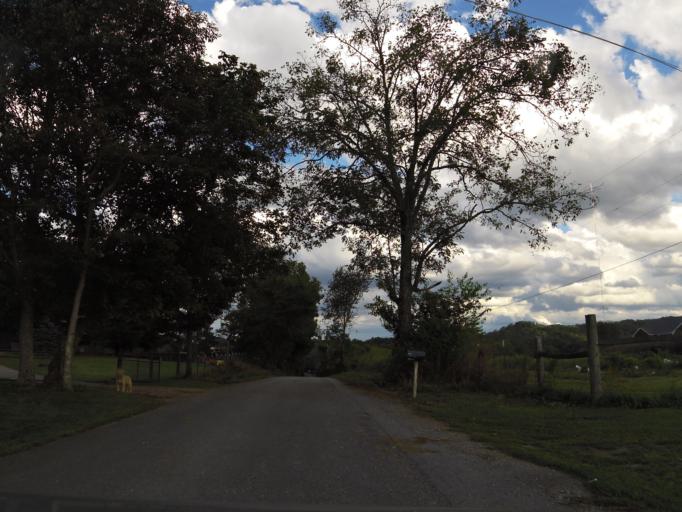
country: US
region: Tennessee
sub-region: Grainger County
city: Blaine
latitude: 36.1444
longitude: -83.7403
